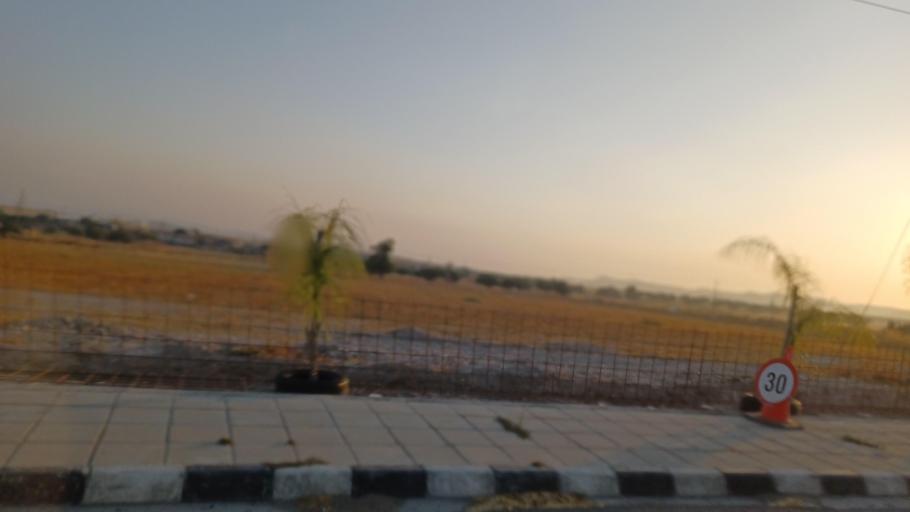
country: CY
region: Larnaka
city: Tersefanou
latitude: 34.8931
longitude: 33.5183
